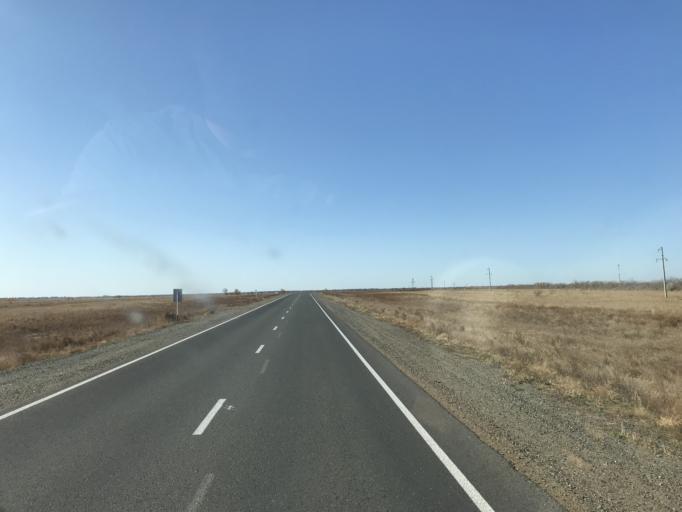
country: KZ
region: Pavlodar
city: Kurchatov
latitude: 51.0257
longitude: 79.1529
